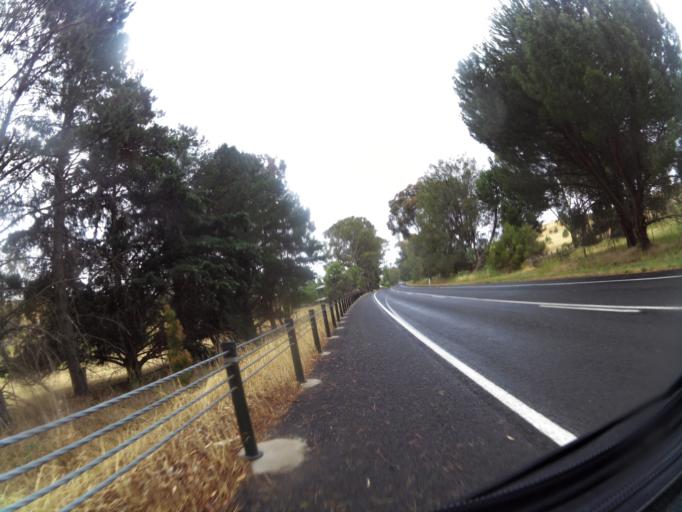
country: AU
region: Victoria
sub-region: Mount Alexander
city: Castlemaine
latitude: -37.1795
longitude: 144.0282
